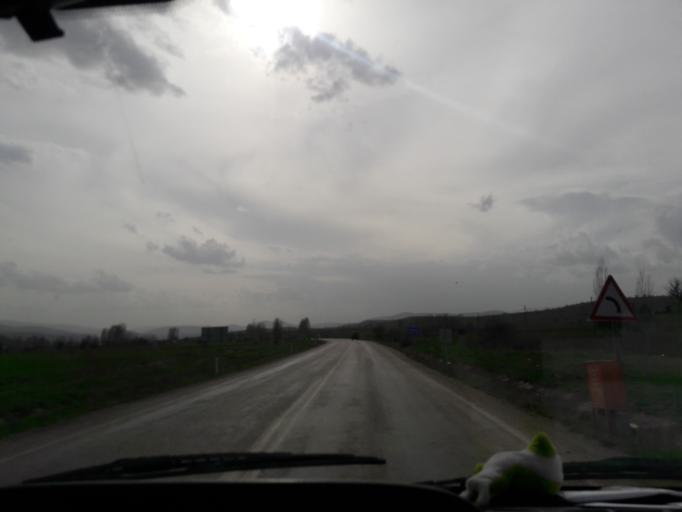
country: TR
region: Gumushane
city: Siran
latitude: 40.1774
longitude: 39.0982
